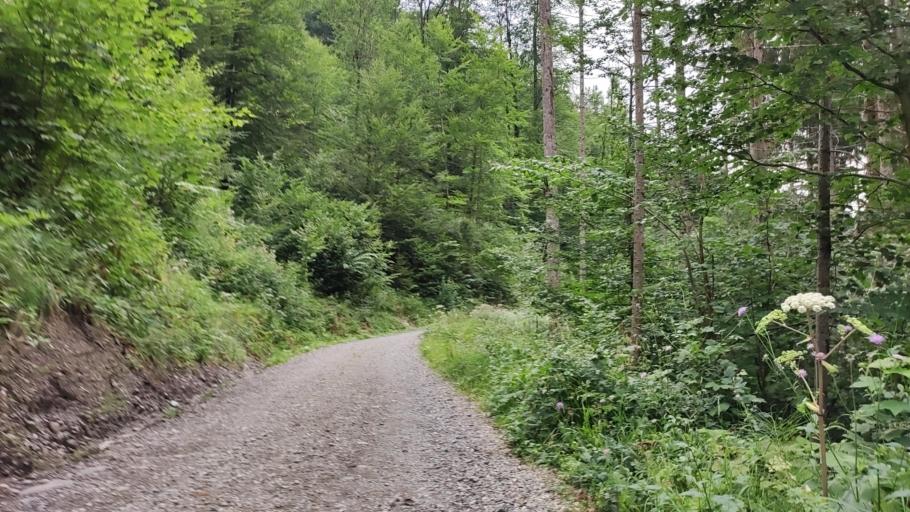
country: AT
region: Vorarlberg
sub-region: Politischer Bezirk Feldkirch
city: Feldkirch
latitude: 47.1924
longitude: 9.6034
